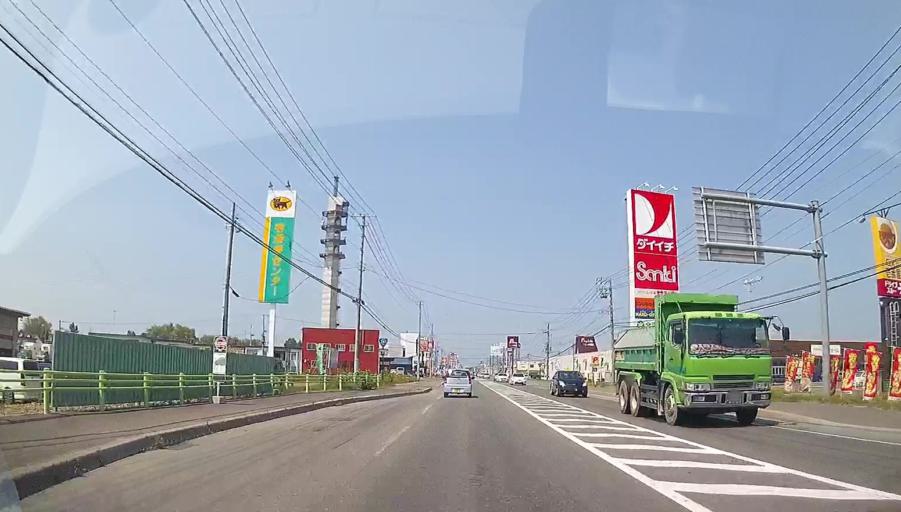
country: JP
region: Hokkaido
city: Otofuke
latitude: 42.9580
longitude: 143.2060
